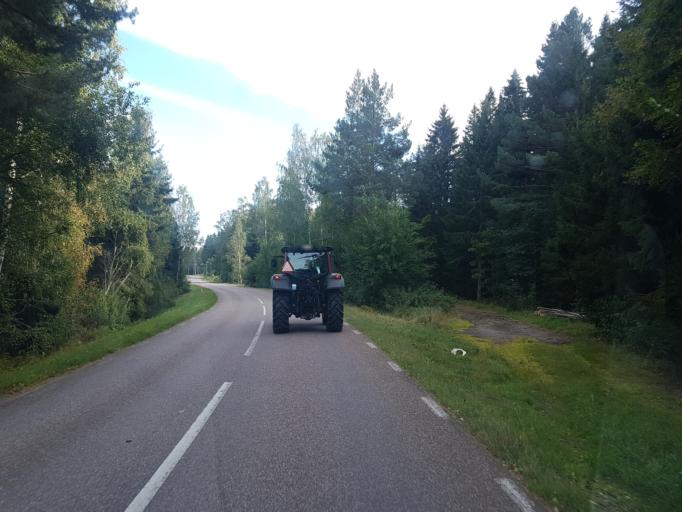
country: SE
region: Dalarna
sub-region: Saters Kommun
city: Saeter
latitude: 60.3658
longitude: 15.7177
